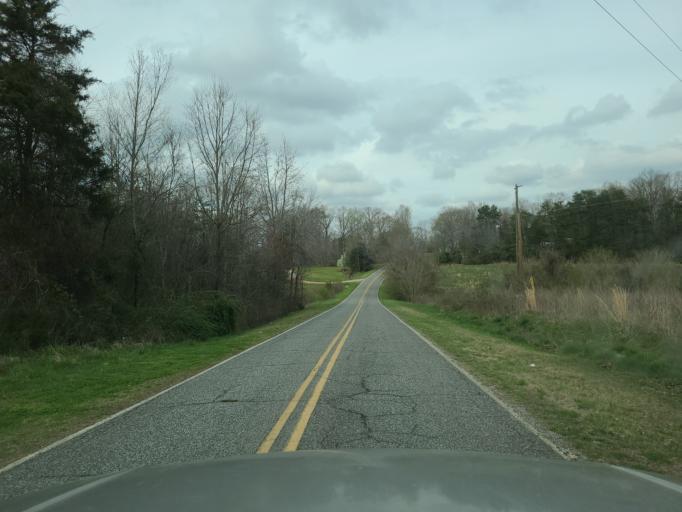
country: US
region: North Carolina
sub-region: Cleveland County
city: Boiling Springs
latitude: 35.2325
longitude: -81.7277
